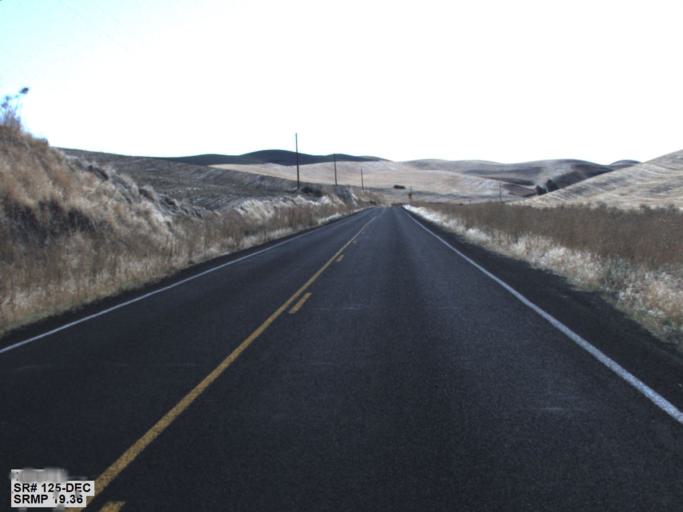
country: US
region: Washington
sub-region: Walla Walla County
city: Walla Walla
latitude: 46.2405
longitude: -118.3677
